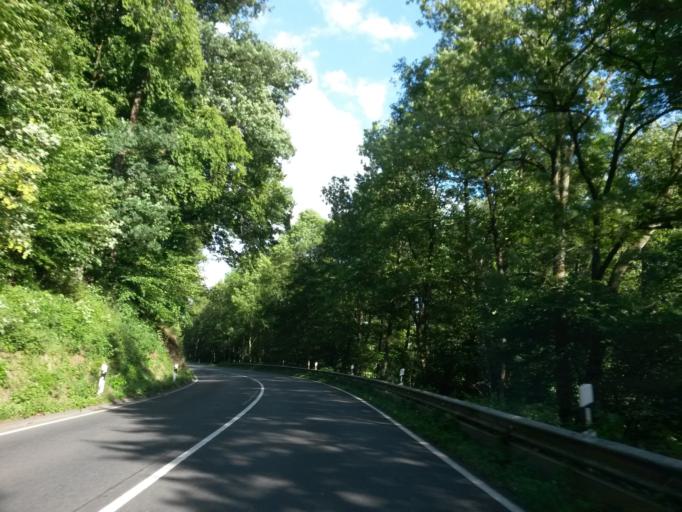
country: DE
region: North Rhine-Westphalia
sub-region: Regierungsbezirk Koln
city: Ruppichteroth
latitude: 50.8389
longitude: 7.4459
